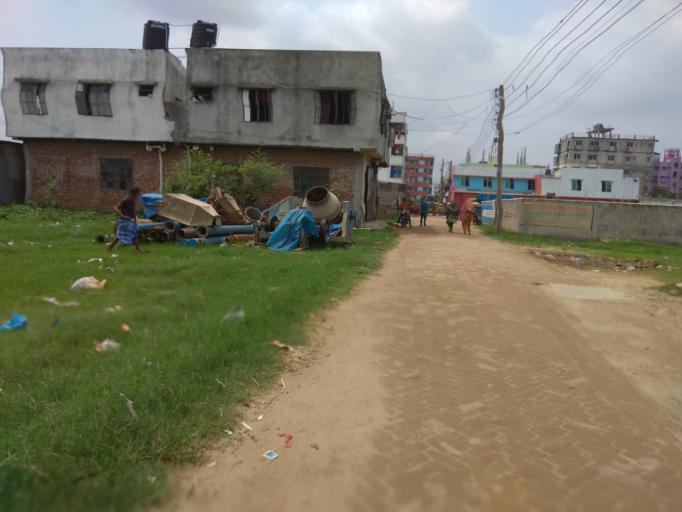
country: BD
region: Dhaka
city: Tungi
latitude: 23.8276
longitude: 90.3538
